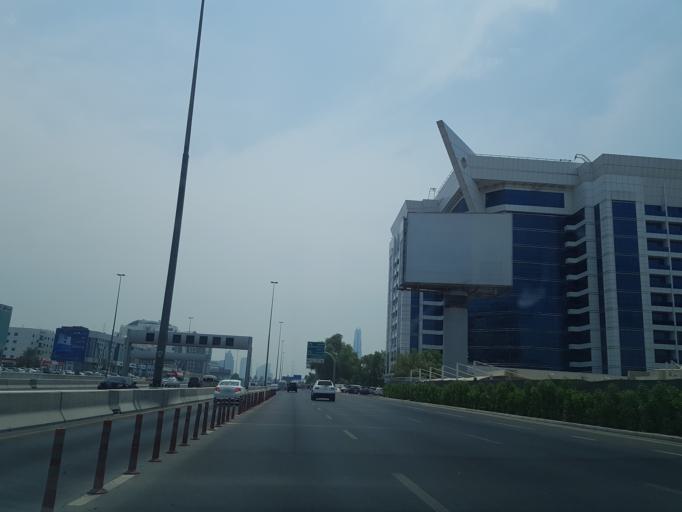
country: AE
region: Ash Shariqah
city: Sharjah
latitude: 25.2476
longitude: 55.3369
